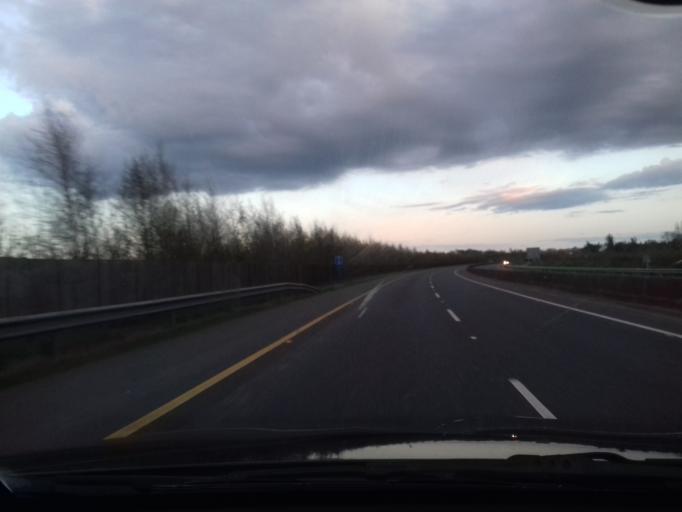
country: IE
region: Leinster
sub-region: An Mhi
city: Navan
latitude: 53.6683
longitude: -6.7643
